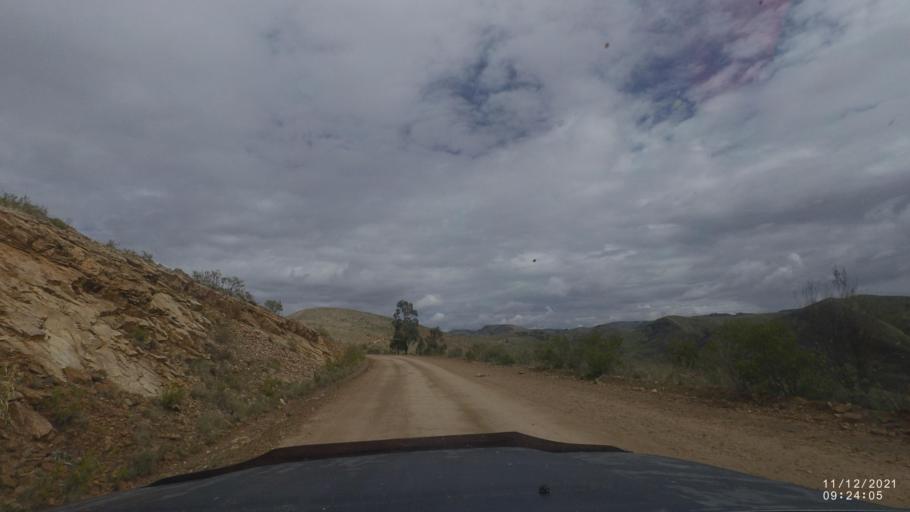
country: BO
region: Cochabamba
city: Tarata
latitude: -17.8747
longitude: -65.9813
